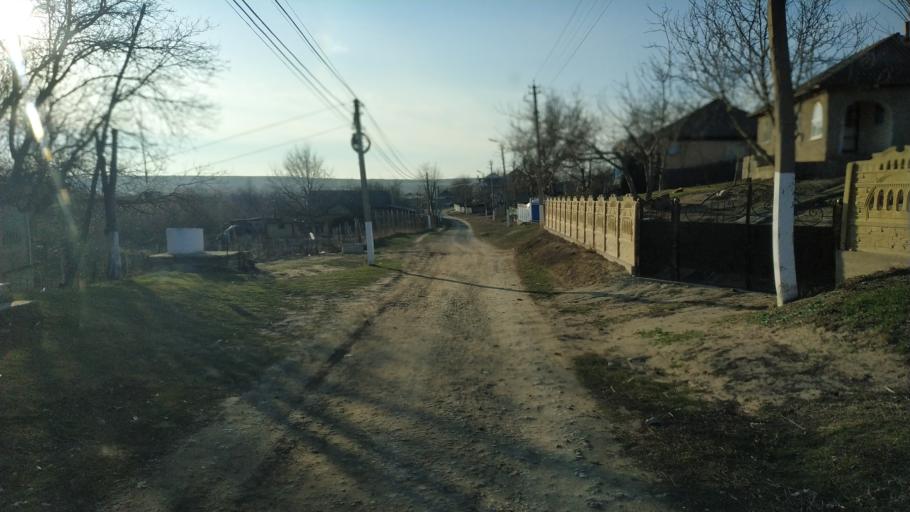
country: MD
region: Hincesti
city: Hincesti
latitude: 46.6996
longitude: 28.5348
